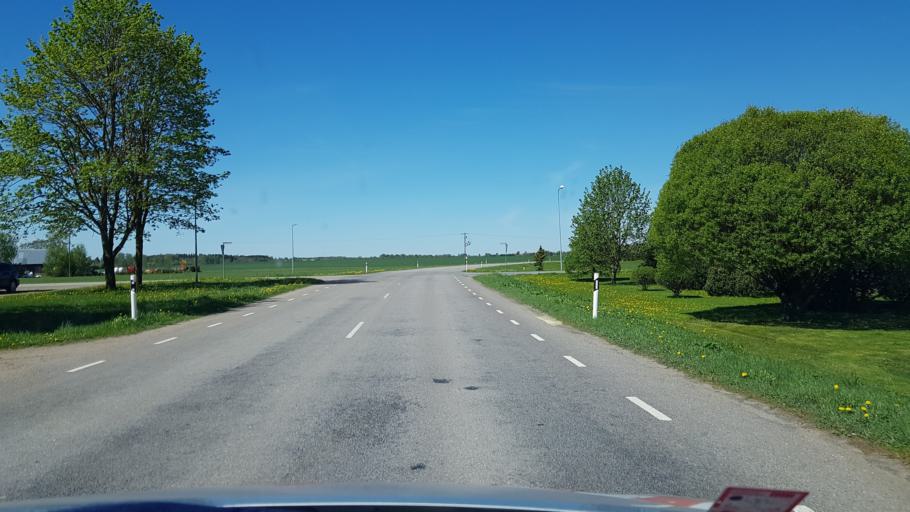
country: EE
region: Tartu
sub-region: Tartu linn
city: Tartu
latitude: 58.3819
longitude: 26.6180
